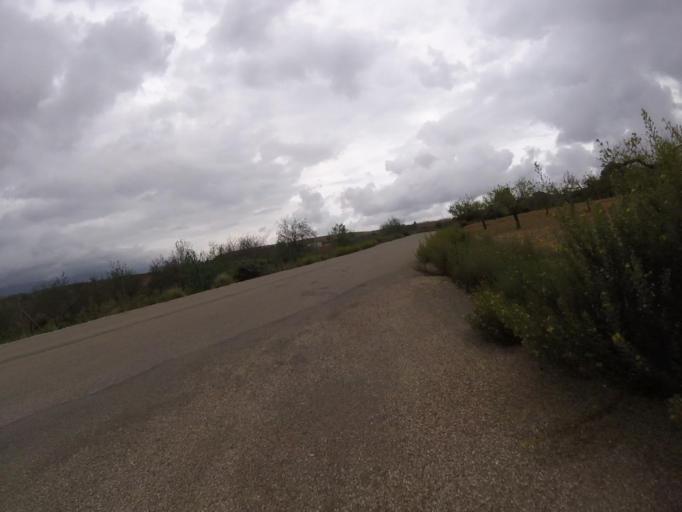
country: ES
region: Valencia
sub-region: Provincia de Castello
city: Benlloch
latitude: 40.2004
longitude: 0.0562
